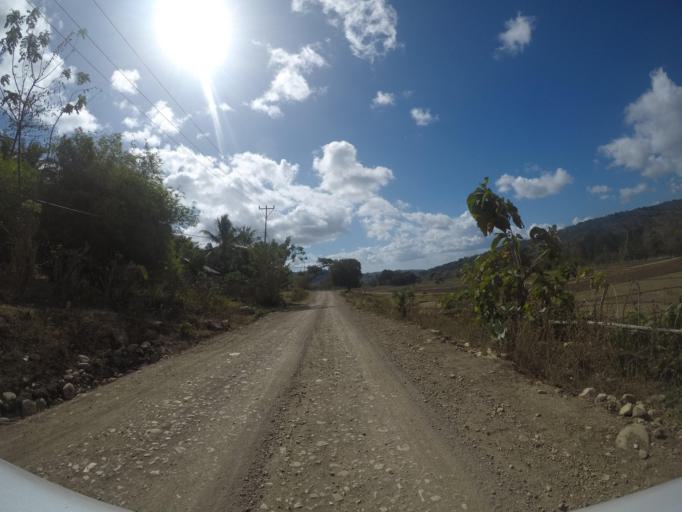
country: TL
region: Lautem
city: Lospalos
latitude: -8.5216
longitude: 126.8408
